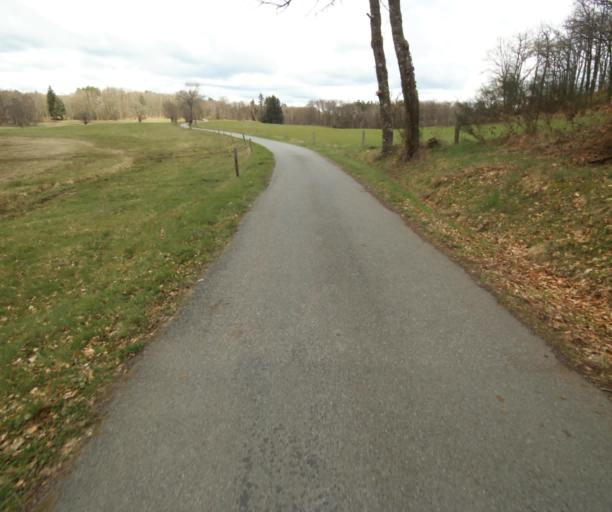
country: FR
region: Limousin
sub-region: Departement de la Correze
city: Correze
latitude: 45.3195
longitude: 1.8916
